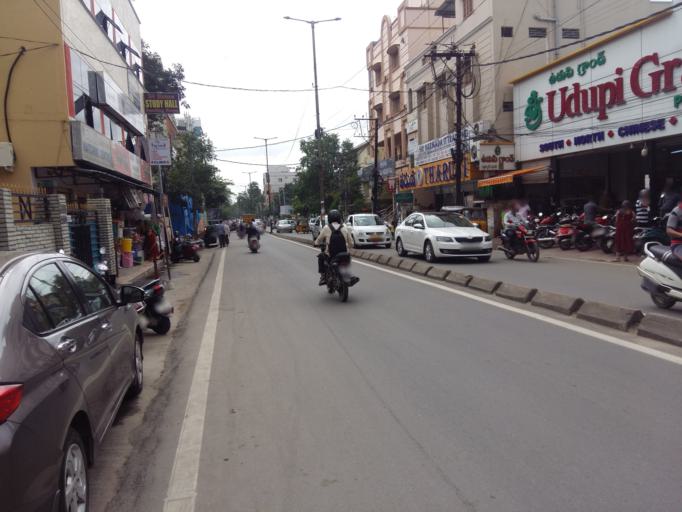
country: IN
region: Telangana
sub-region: Rangareddi
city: Kukatpalli
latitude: 17.4929
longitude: 78.4098
